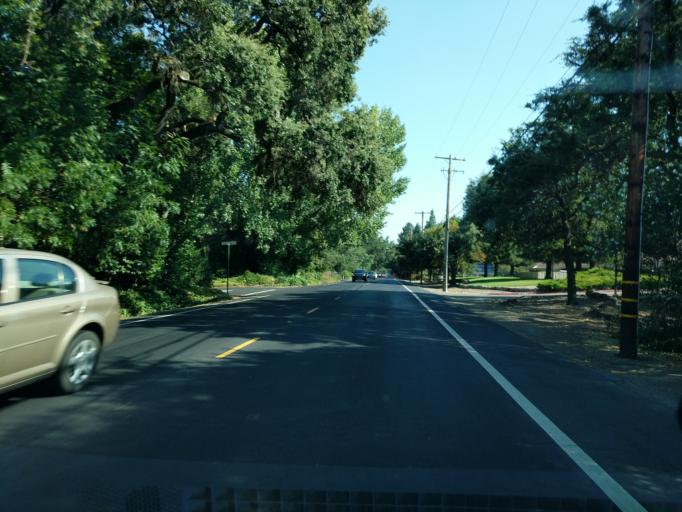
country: US
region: California
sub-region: Contra Costa County
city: Alamo
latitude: 37.8678
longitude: -122.0437
